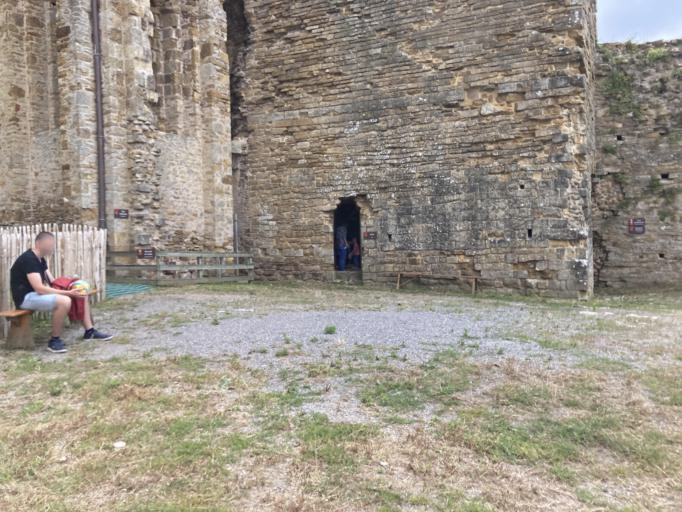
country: FR
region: Pays de la Loire
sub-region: Departement de la Vendee
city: Saint-Hilaire-de-Talmont
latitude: 46.4675
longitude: -1.6194
